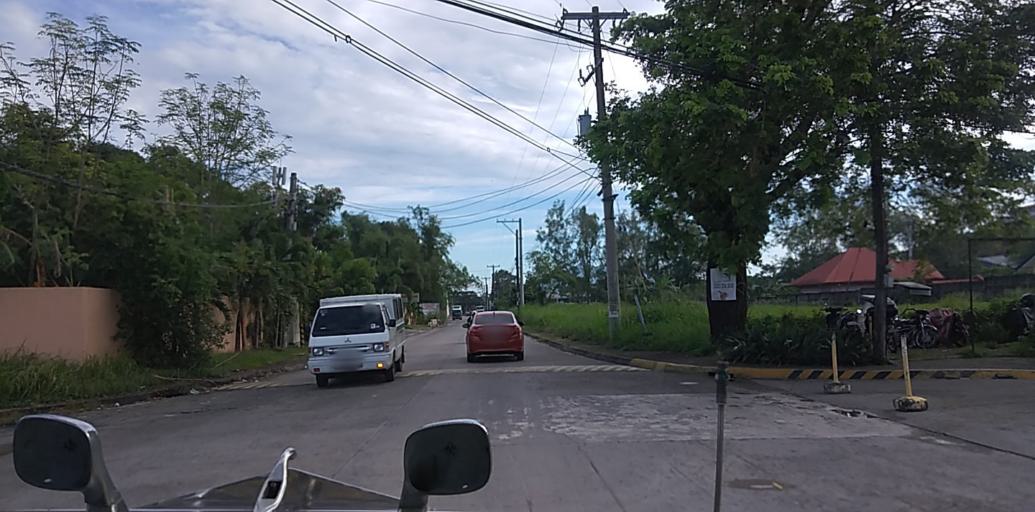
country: PH
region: Central Luzon
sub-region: Province of Pampanga
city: Telabastagan
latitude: 15.1076
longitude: 120.6109
